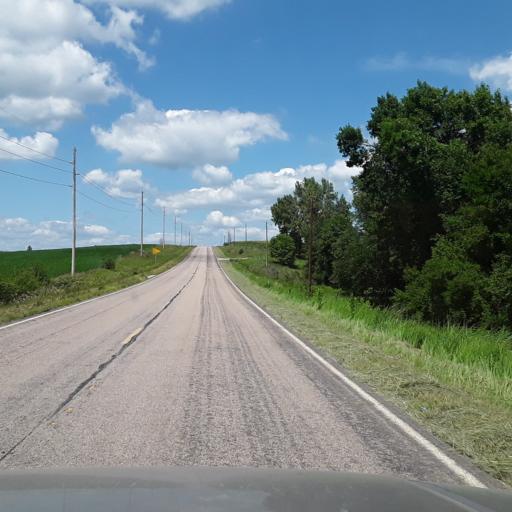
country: US
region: Nebraska
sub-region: Nance County
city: Genoa
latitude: 41.5151
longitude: -97.6960
